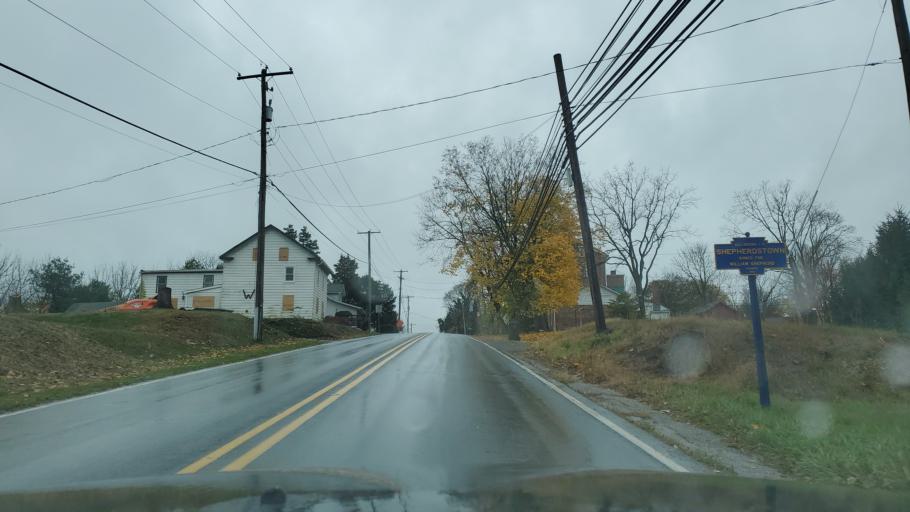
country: US
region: Pennsylvania
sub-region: Cumberland County
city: Mechanicsburg
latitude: 40.1789
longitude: -76.9904
